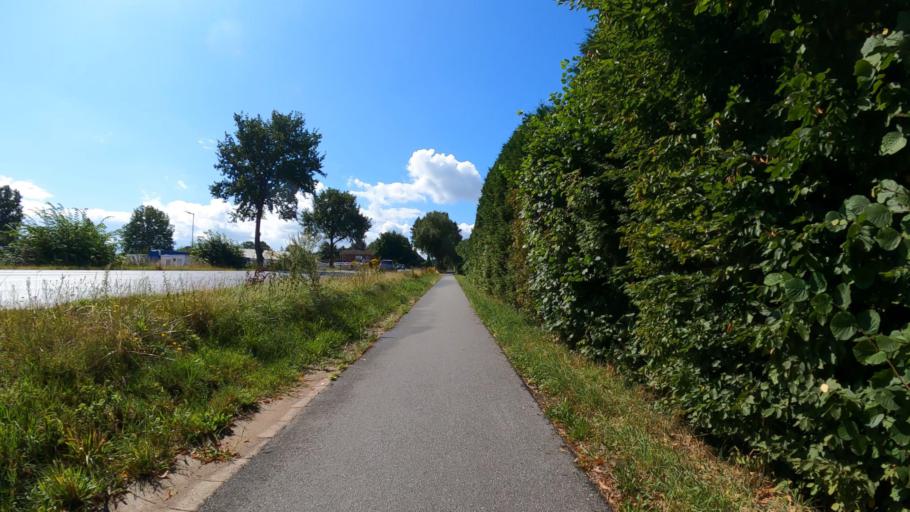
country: DE
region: Schleswig-Holstein
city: Fuhlendorf
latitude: 53.9442
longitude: 9.8967
